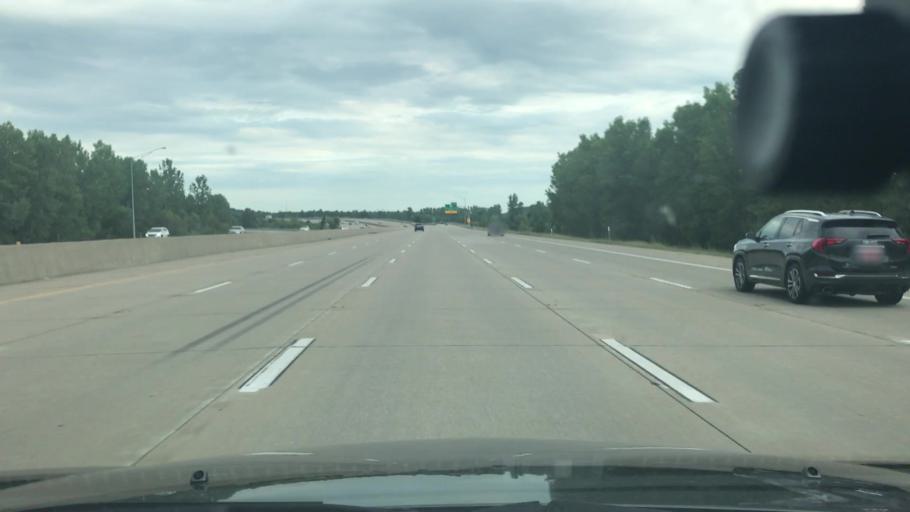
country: US
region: Missouri
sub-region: Saint Charles County
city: Saint Charles
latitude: 38.7142
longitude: -90.5080
